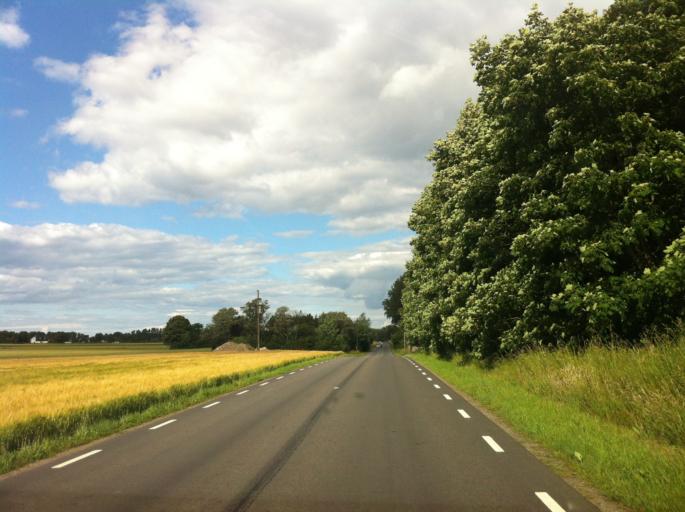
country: SE
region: Skane
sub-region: Simrishamns Kommun
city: Simrishamn
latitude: 55.4342
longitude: 14.2274
